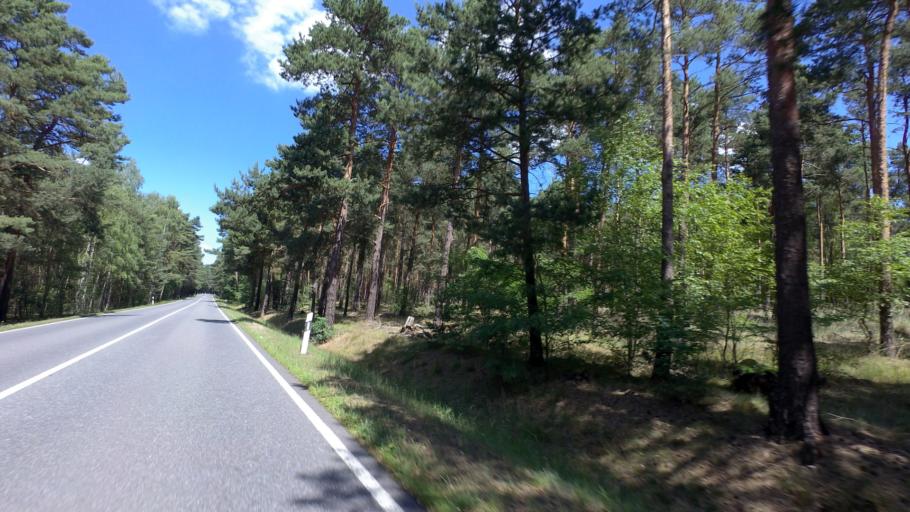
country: DE
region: Brandenburg
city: Kasel-Golzig
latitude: 51.9184
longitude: 13.6680
